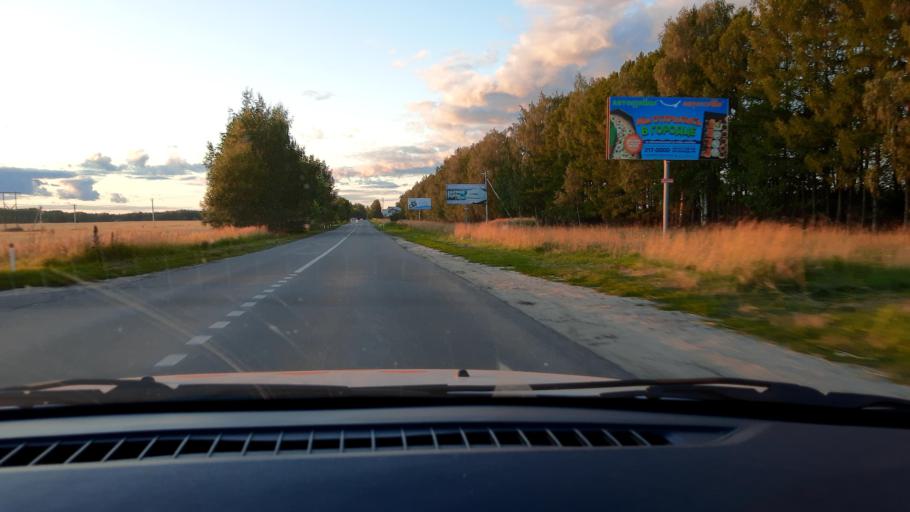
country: RU
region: Nizjnij Novgorod
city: Zavolzh'ye
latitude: 56.6936
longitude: 43.4175
